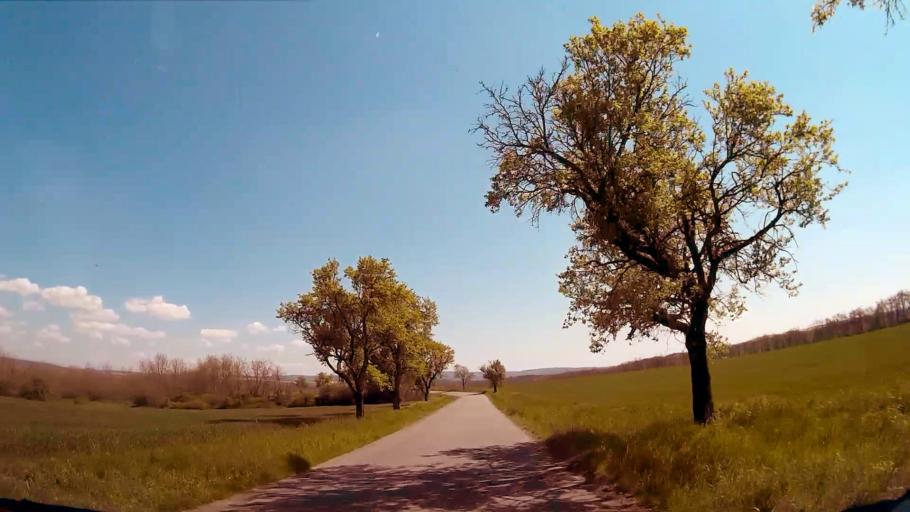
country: CZ
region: South Moravian
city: Moravsky Krumlov
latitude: 49.0753
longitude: 16.3086
